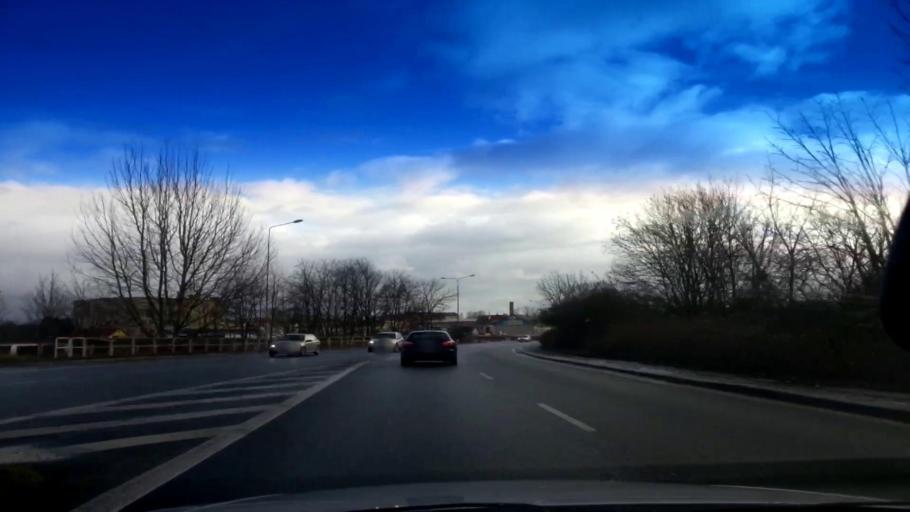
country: CZ
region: Karlovarsky
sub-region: Okres Cheb
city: Cheb
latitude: 50.0836
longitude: 12.3728
